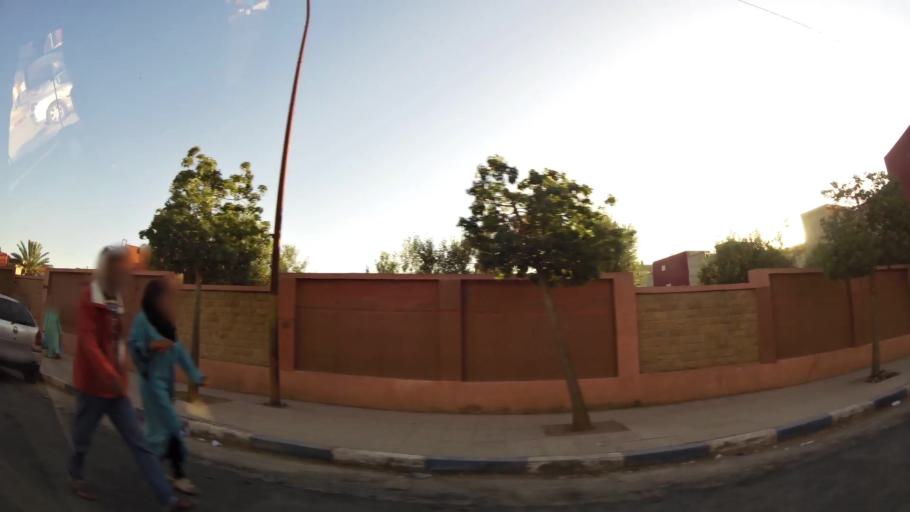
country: MA
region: Oriental
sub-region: Berkane-Taourirt
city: Berkane
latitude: 34.9230
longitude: -2.3177
